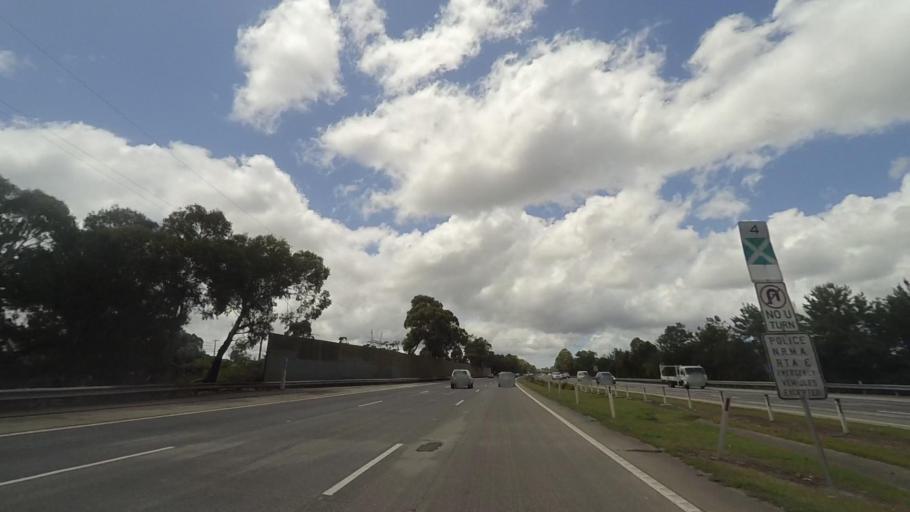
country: AU
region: New South Wales
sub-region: Hornsby Shire
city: Mount Colah
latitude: -33.6620
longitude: 151.1269
